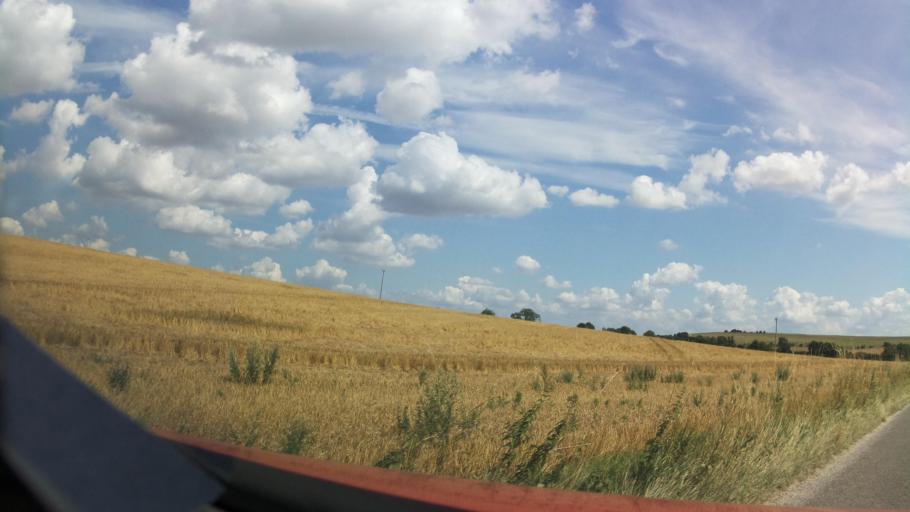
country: GB
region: England
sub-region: West Berkshire
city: Lambourn
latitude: 51.5240
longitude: -1.5785
